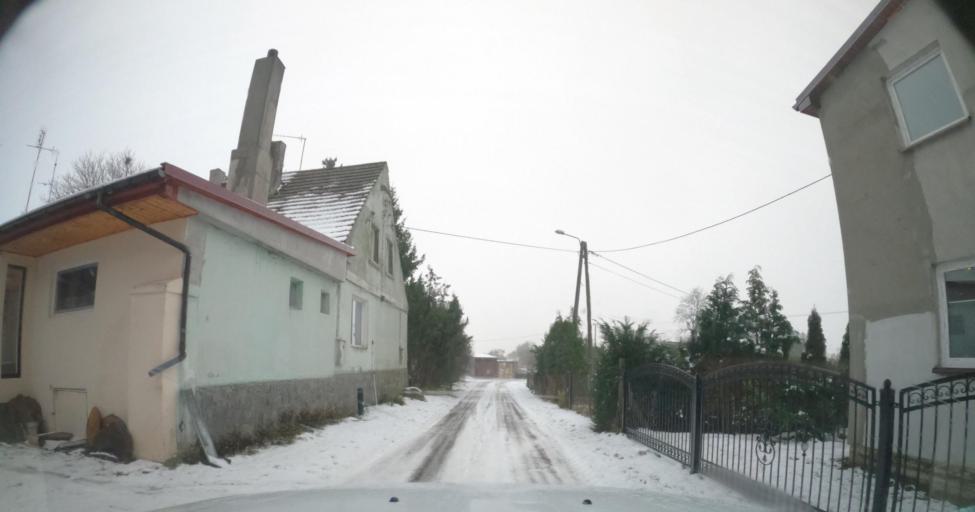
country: PL
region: West Pomeranian Voivodeship
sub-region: Powiat kamienski
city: Golczewo
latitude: 53.7887
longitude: 14.9536
